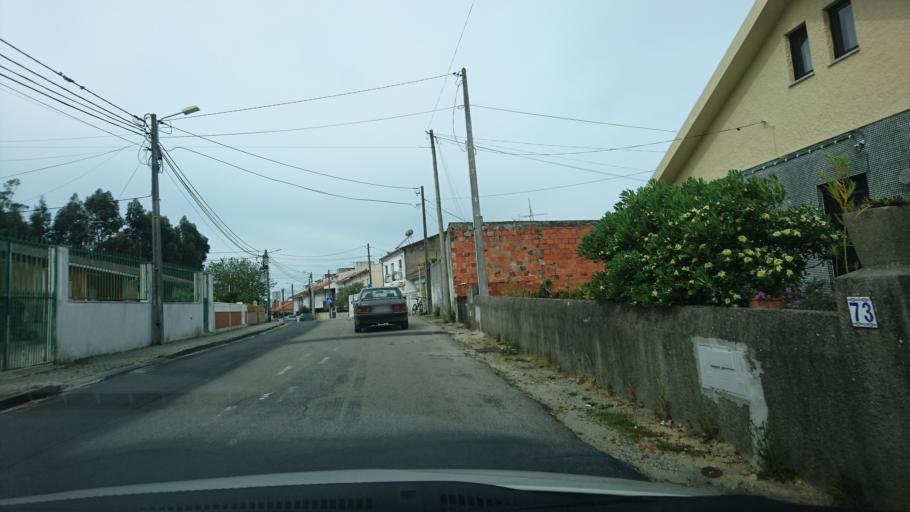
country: PT
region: Aveiro
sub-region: Aveiro
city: Aveiro
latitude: 40.6448
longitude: -8.6147
